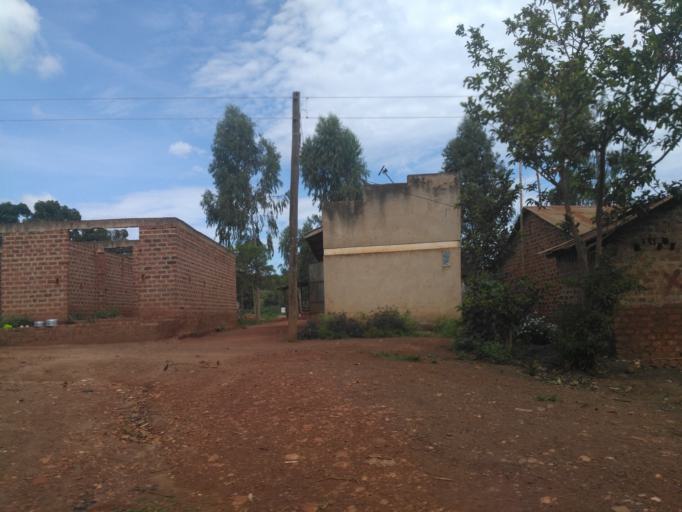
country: UG
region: Central Region
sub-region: Buikwe District
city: Njeru
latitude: 0.3947
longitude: 33.1727
